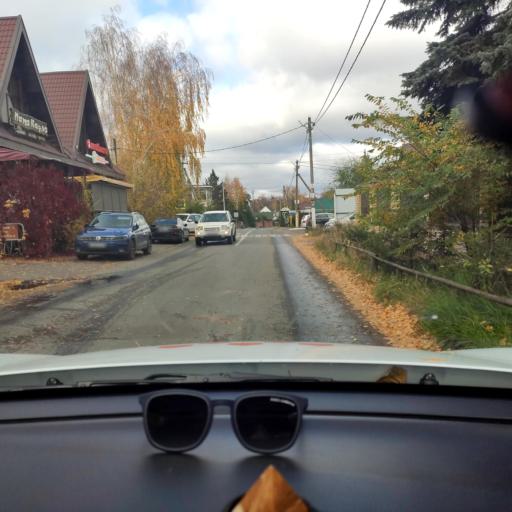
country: RU
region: Tatarstan
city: Verkhniy Uslon
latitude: 55.6211
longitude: 49.0142
